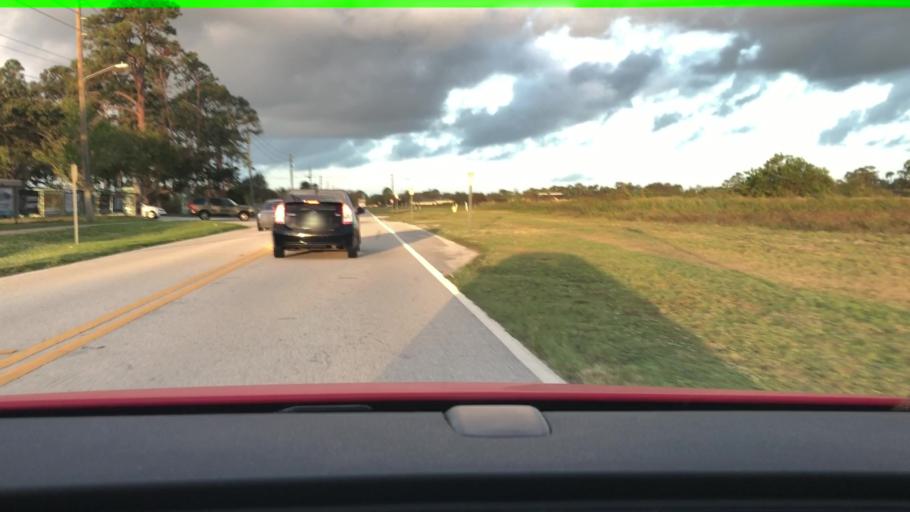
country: US
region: Florida
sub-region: Volusia County
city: South Daytona
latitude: 29.1503
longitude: -81.0275
